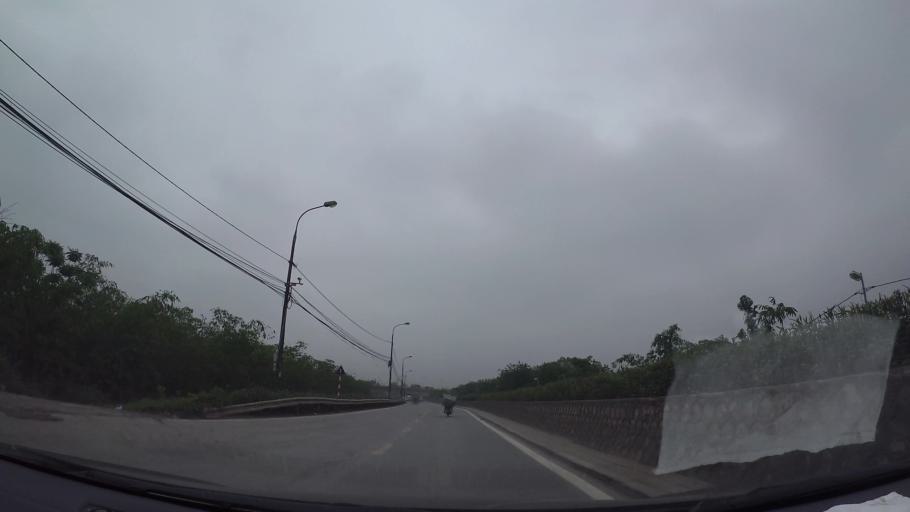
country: VN
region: Hung Yen
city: Van Giang
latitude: 20.9828
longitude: 105.8948
